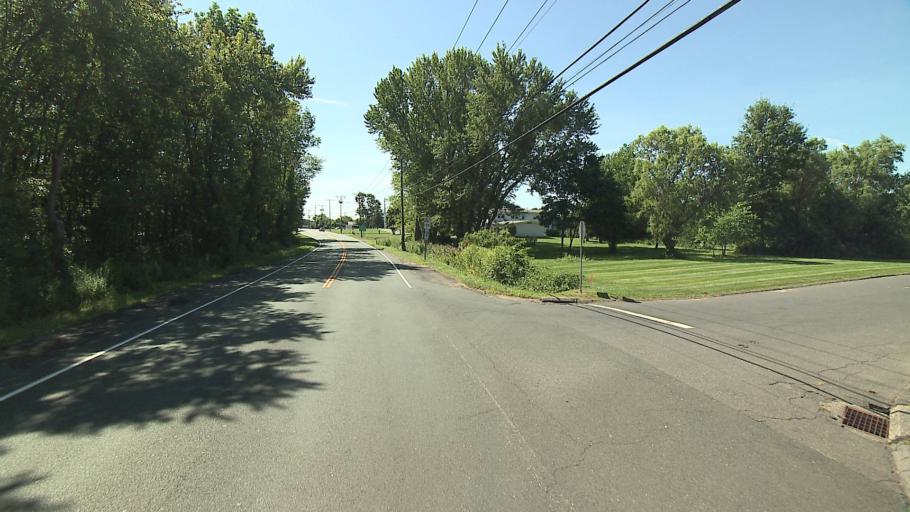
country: US
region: Connecticut
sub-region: Hartford County
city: Blue Hills
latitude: 41.8373
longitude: -72.6995
